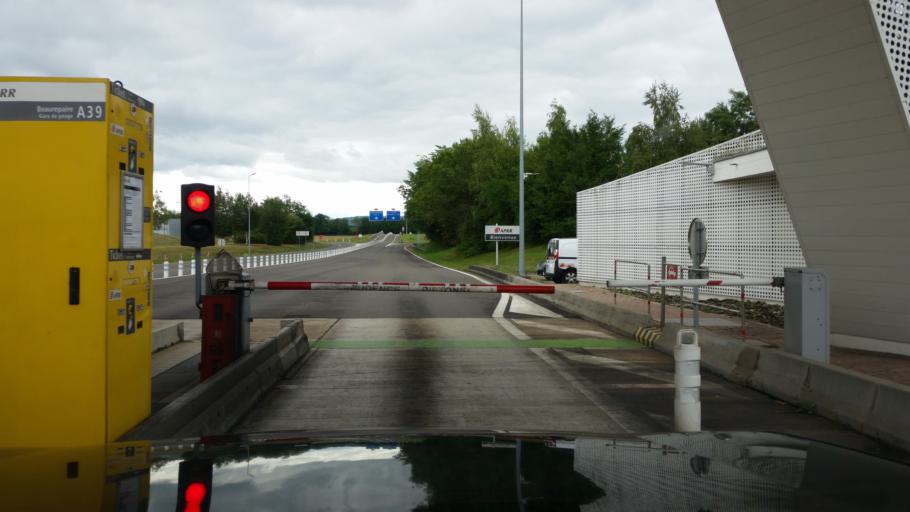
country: FR
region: Franche-Comte
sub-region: Departement du Jura
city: Bletterans
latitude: 46.6663
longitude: 5.4189
